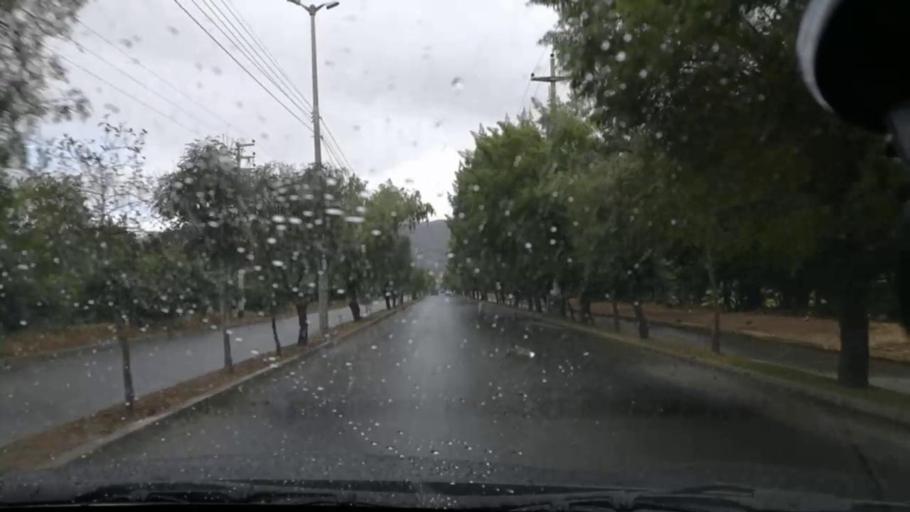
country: PE
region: Cajamarca
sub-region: Provincia de Cajamarca
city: Cajamarca
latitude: -7.1652
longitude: -78.4865
